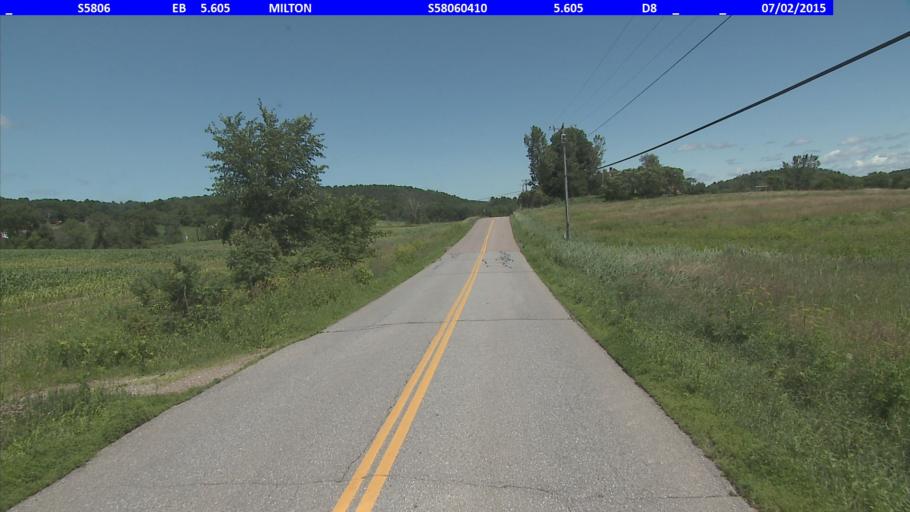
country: US
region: Vermont
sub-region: Chittenden County
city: Milton
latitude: 44.7011
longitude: -73.1806
